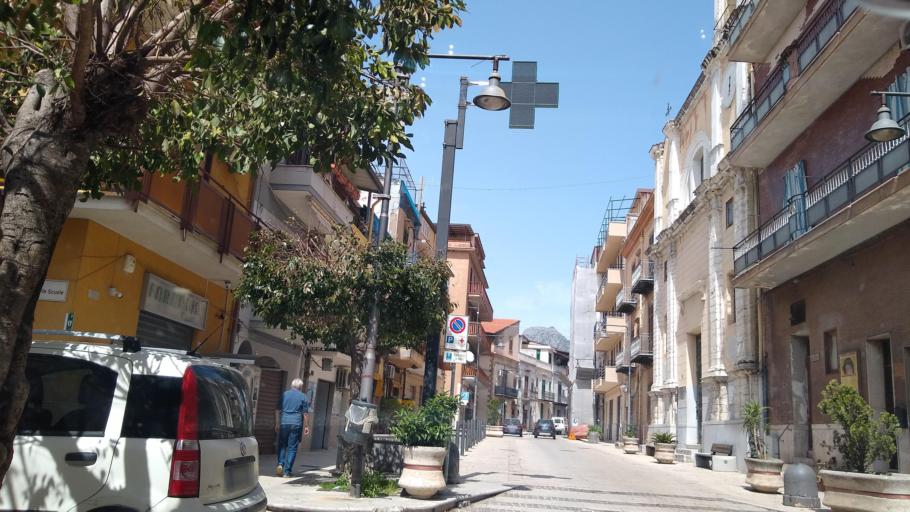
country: IT
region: Sicily
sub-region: Palermo
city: San Giuseppe Jato
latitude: 37.9694
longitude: 13.1822
